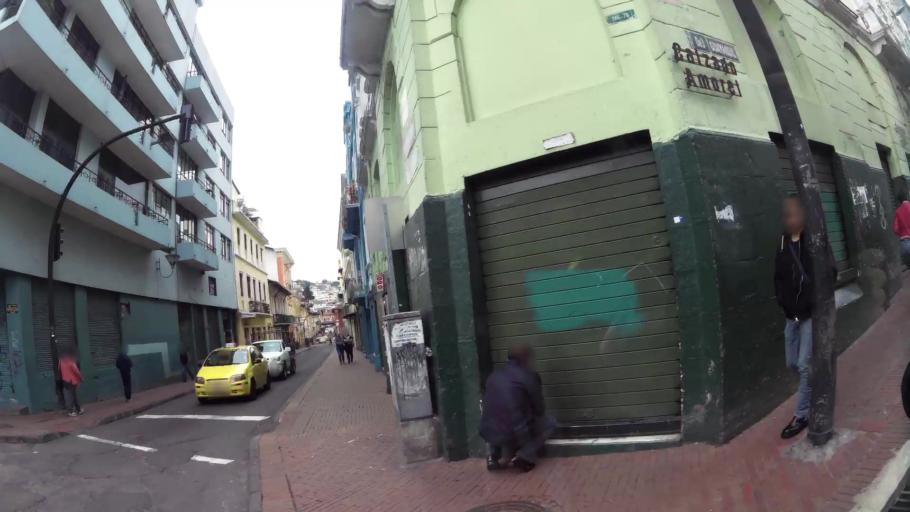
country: EC
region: Pichincha
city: Quito
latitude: -0.2193
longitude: -78.5098
